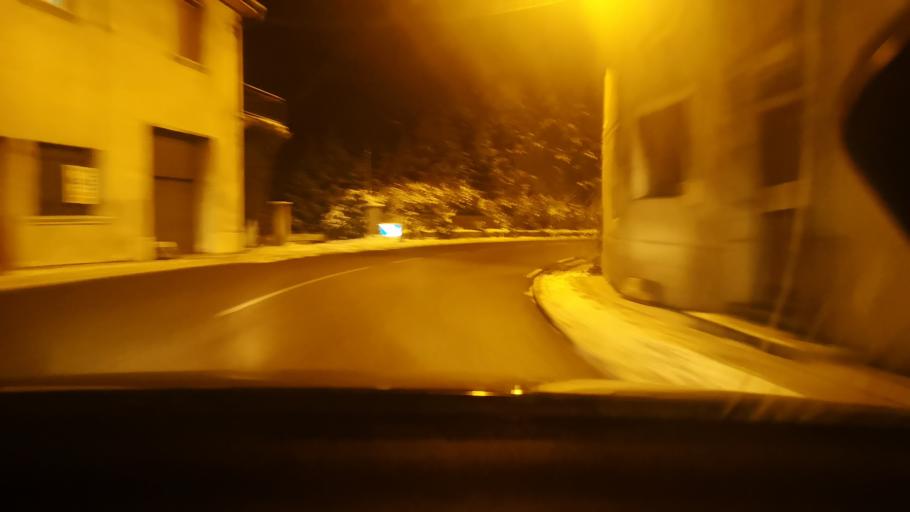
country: FR
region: Rhone-Alpes
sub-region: Departement de l'Ain
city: Nantua
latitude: 46.1391
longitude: 5.6265
